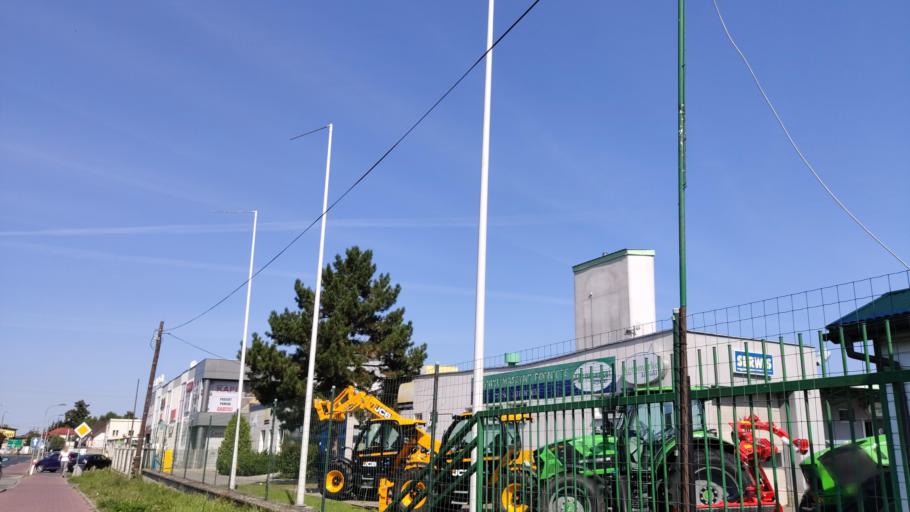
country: PL
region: Kujawsko-Pomorskie
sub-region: Powiat zninski
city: Znin
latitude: 52.8458
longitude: 17.7415
